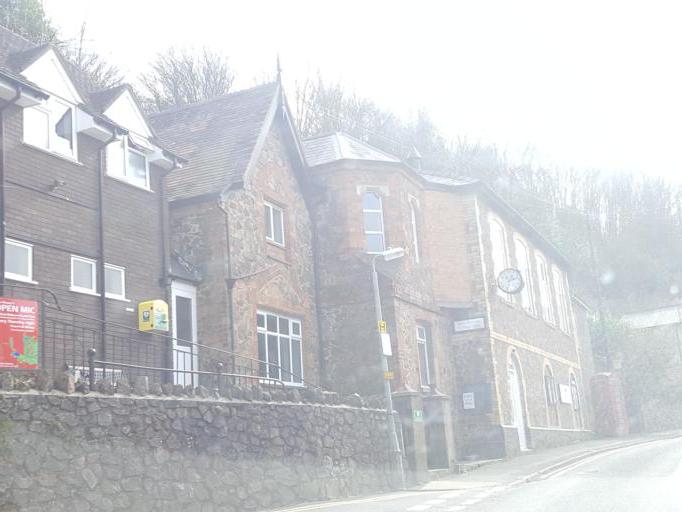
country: GB
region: England
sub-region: Worcestershire
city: Great Malvern
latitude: 52.1182
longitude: -2.3451
